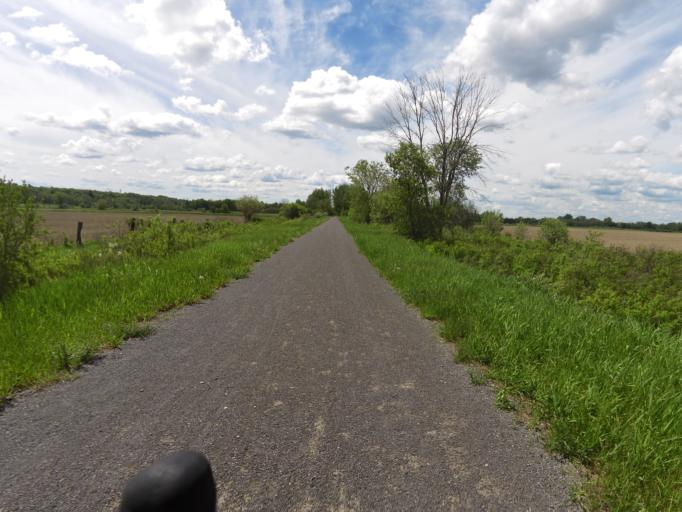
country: CA
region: Ontario
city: Ottawa
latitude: 45.4146
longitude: -75.5822
